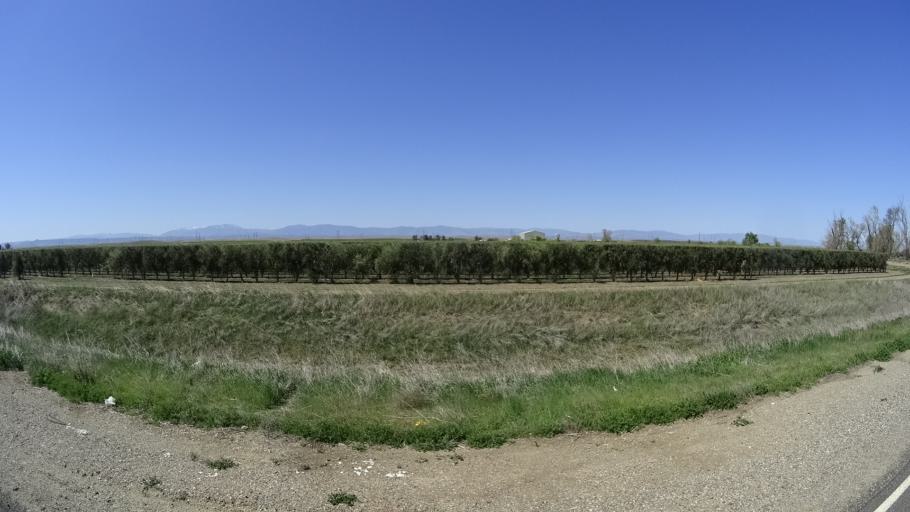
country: US
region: California
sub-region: Glenn County
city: Willows
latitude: 39.6046
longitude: -122.2499
